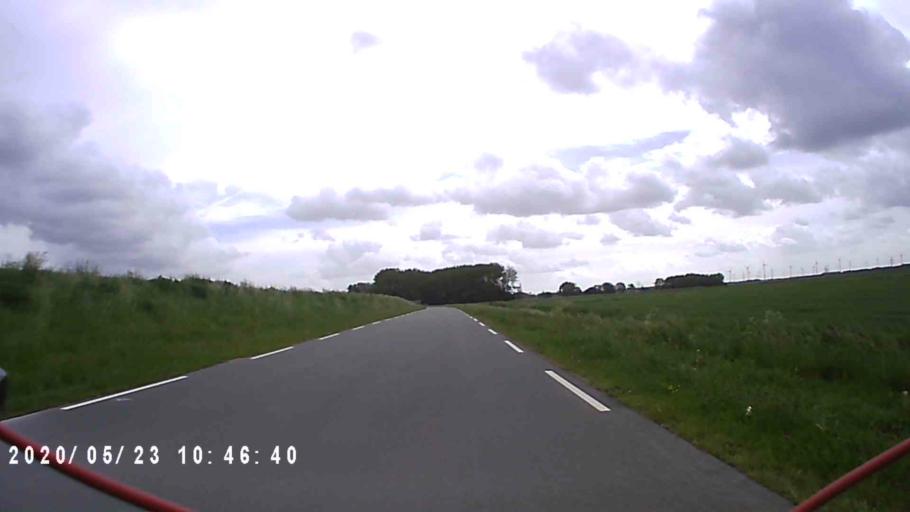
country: NL
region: Groningen
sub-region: Gemeente Delfzijl
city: Delfzijl
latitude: 53.3117
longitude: 6.9200
